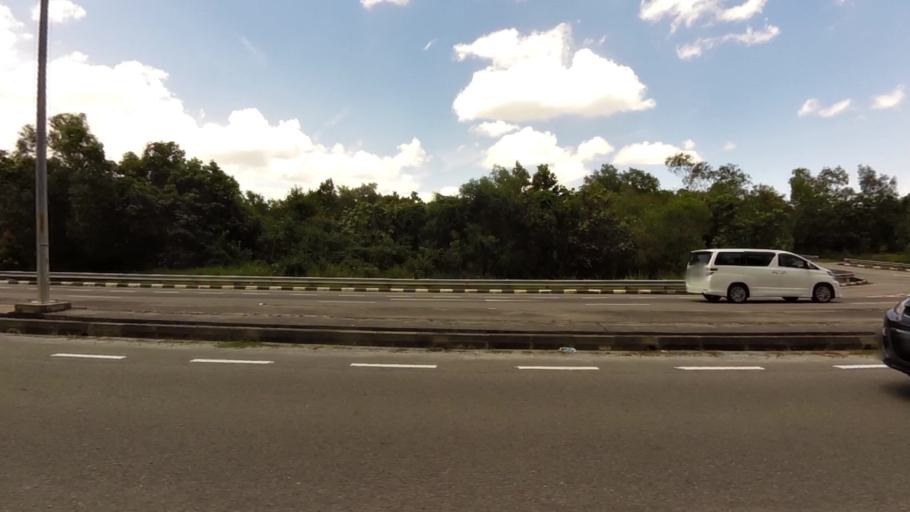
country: BN
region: Brunei and Muara
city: Bandar Seri Begawan
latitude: 4.9345
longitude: 114.9724
